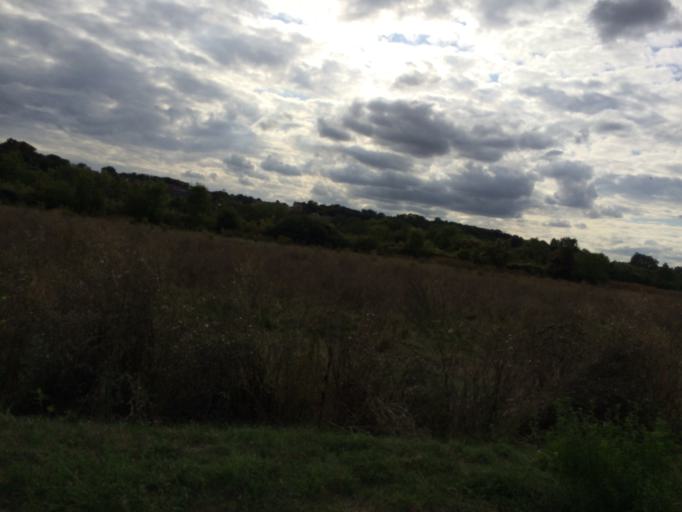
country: FR
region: Ile-de-France
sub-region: Departement de l'Essonne
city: Soisy-sur-Seine
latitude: 48.6508
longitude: 2.4404
